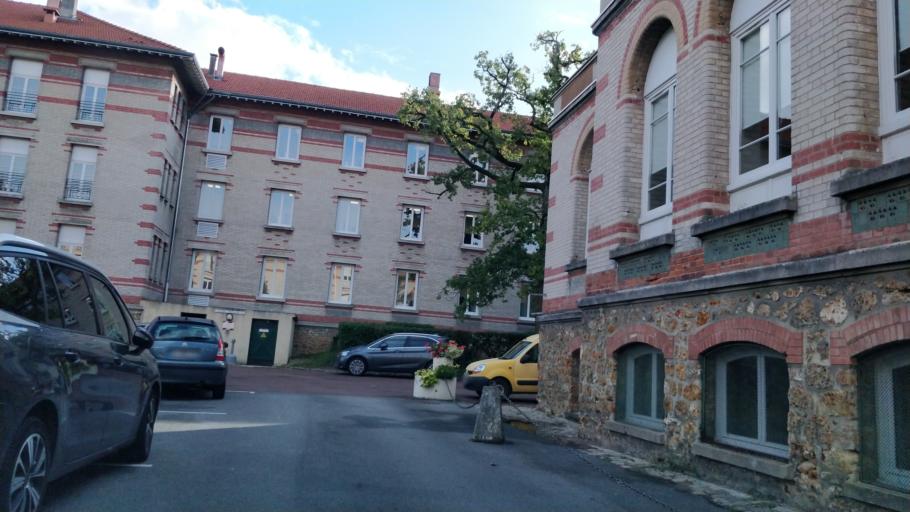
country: FR
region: Ile-de-France
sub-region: Departement de l'Essonne
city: Fontenay-les-Briis
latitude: 48.6236
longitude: 2.1480
